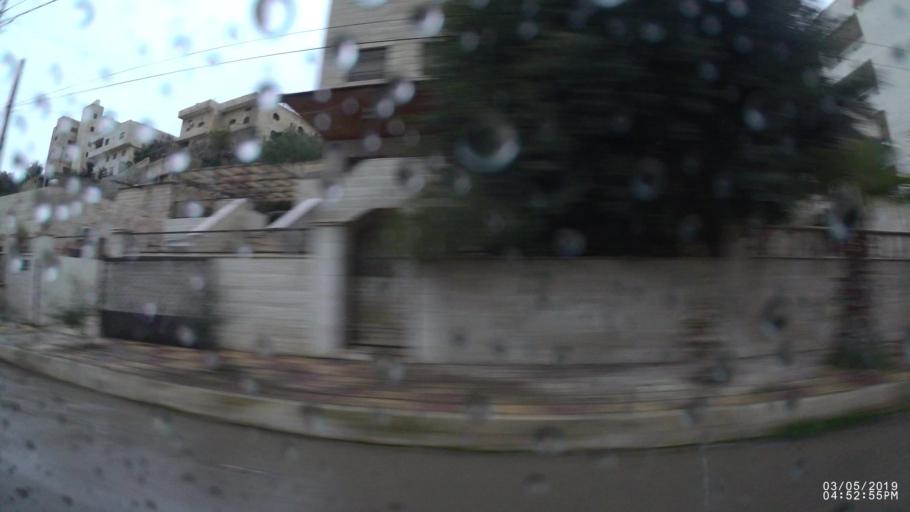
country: JO
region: Amman
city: Amman
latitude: 31.9923
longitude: 35.9737
